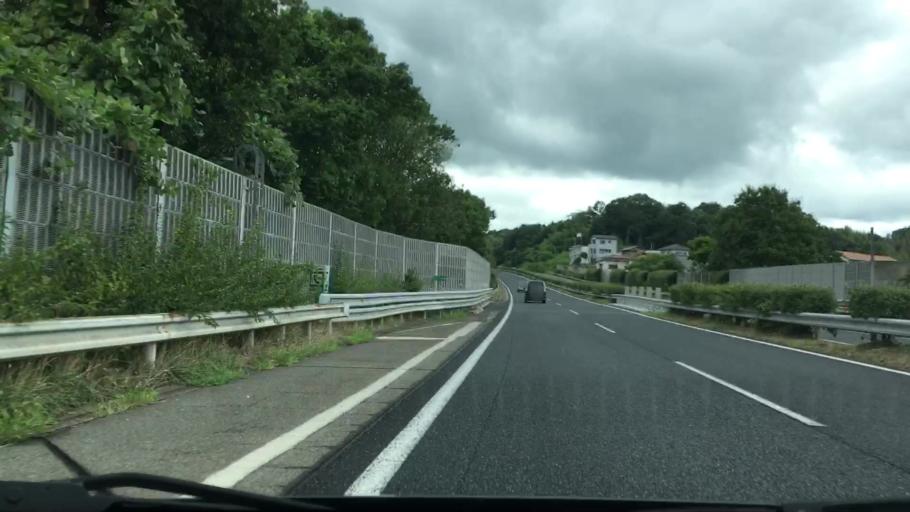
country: JP
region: Okayama
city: Tsuyama
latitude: 35.0755
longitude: 134.0190
